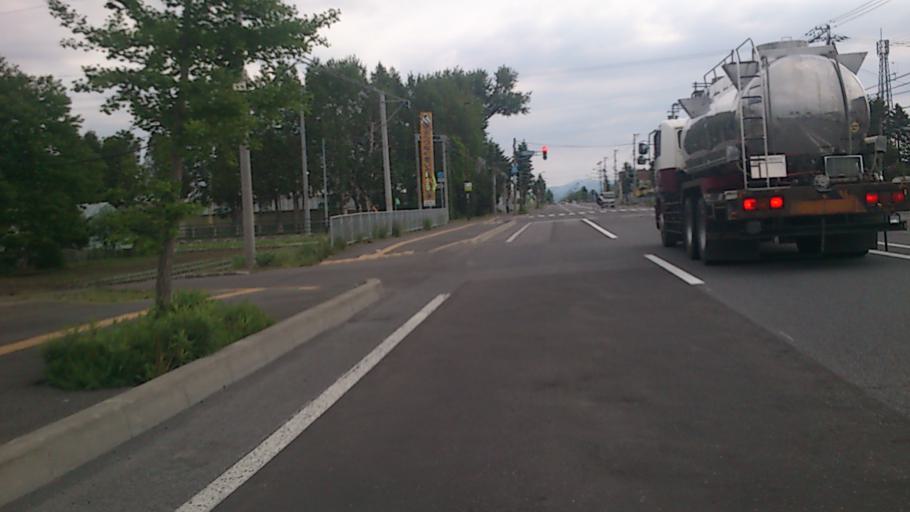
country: JP
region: Hokkaido
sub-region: Asahikawa-shi
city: Asahikawa
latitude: 43.8192
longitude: 142.4477
